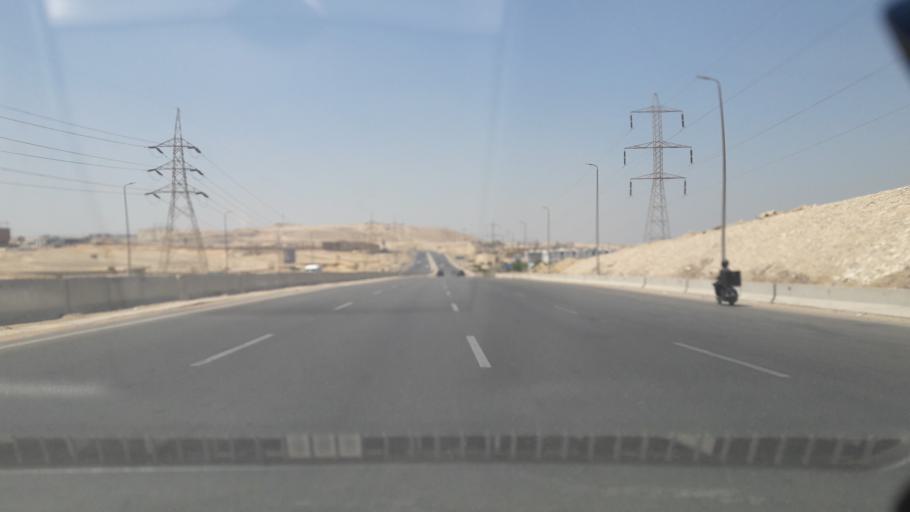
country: EG
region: Al Jizah
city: Awsim
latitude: 30.0137
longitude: 31.0845
